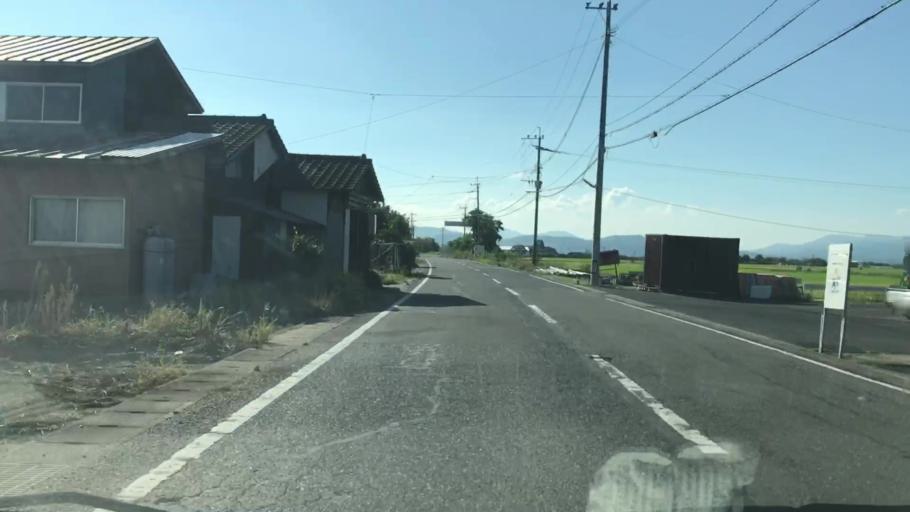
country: JP
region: Saga Prefecture
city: Saga-shi
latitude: 33.1930
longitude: 130.2773
